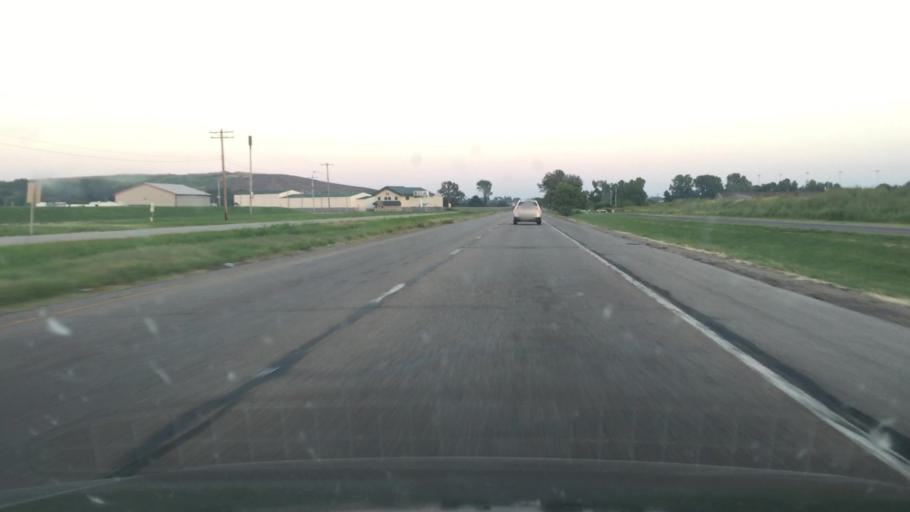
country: US
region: Illinois
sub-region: Madison County
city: Madison
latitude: 38.6624
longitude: -90.1406
